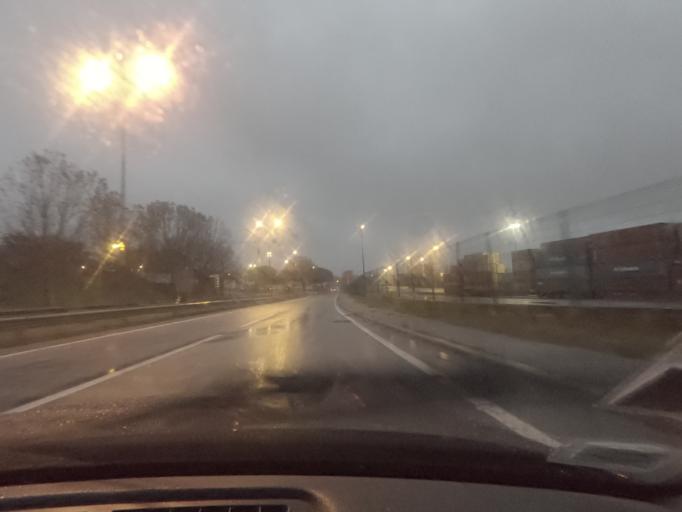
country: PT
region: Porto
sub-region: Matosinhos
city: Matosinhos
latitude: 41.1915
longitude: -8.6809
